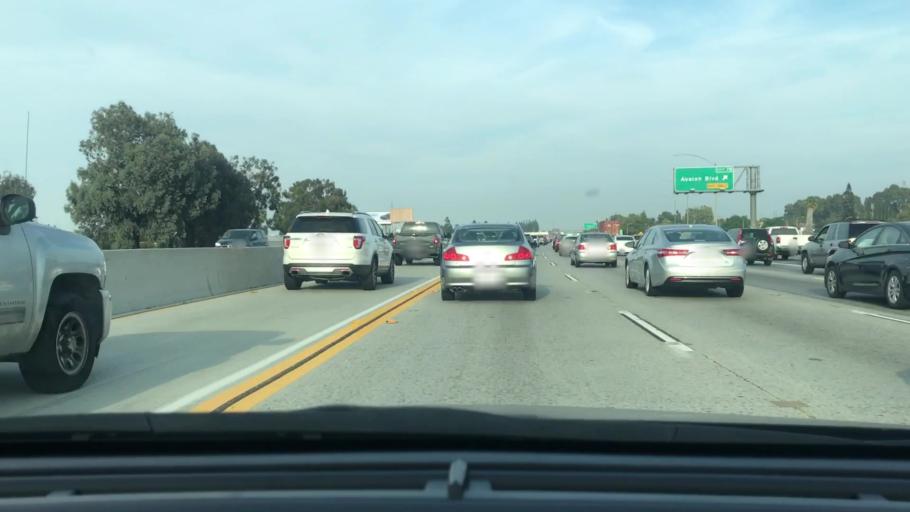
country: US
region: California
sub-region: Los Angeles County
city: West Rancho Dominguez
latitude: 33.8722
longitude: -118.2657
